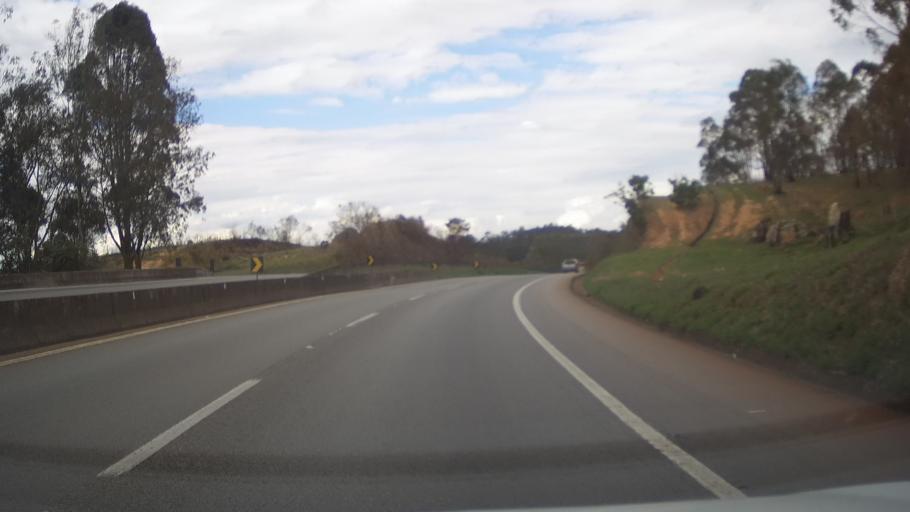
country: BR
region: Minas Gerais
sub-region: Itauna
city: Itauna
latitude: -20.2985
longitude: -44.4404
